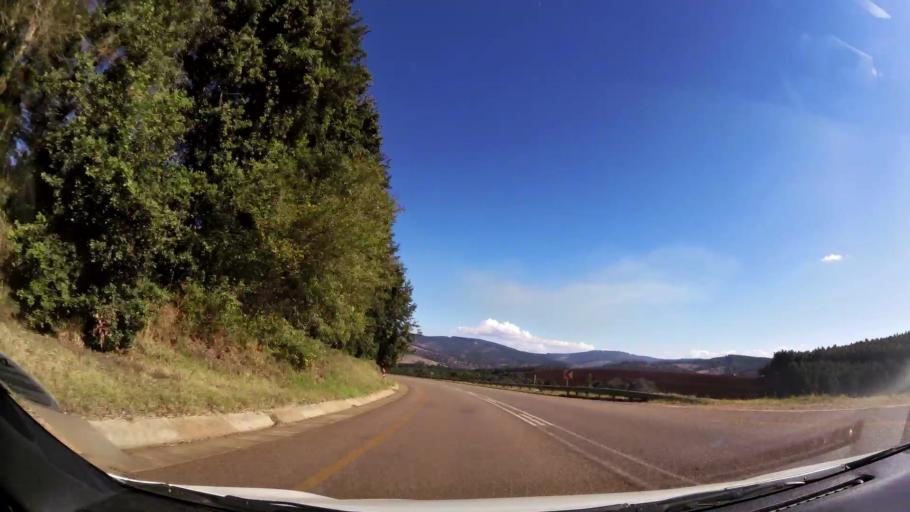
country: ZA
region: Limpopo
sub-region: Capricorn District Municipality
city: Mankoeng
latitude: -23.9285
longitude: 29.9579
